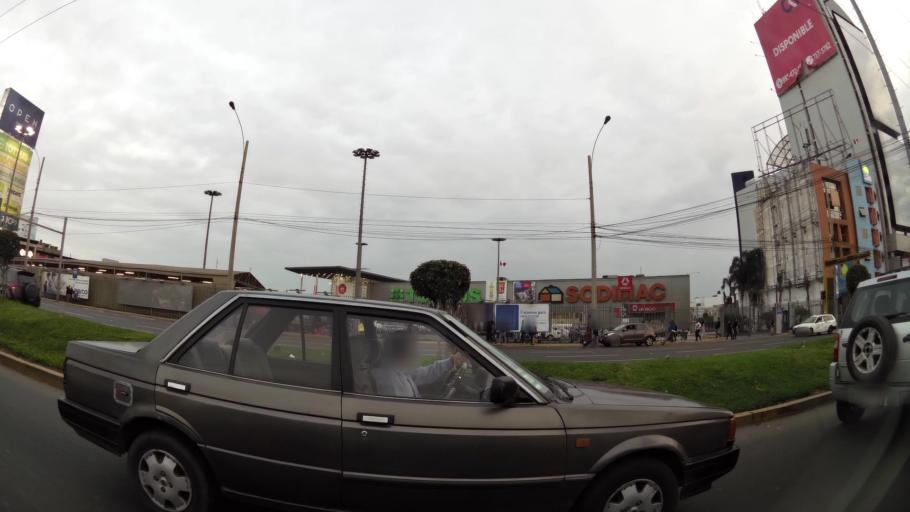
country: PE
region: Callao
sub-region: Callao
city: Callao
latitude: -12.0780
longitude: -77.0882
